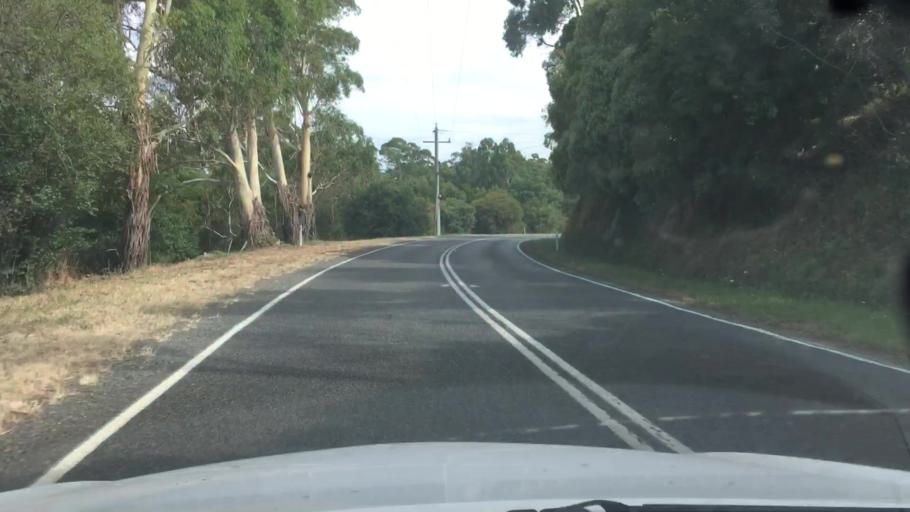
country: AU
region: Victoria
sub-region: Yarra Ranges
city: Woori Yallock
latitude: -37.7936
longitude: 145.5218
